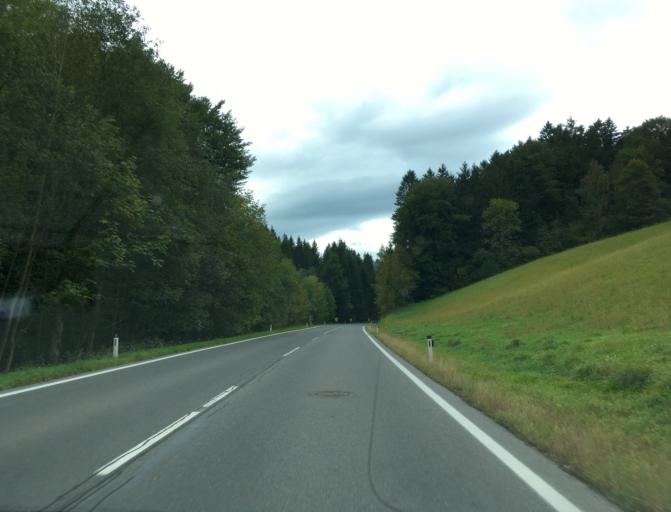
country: AT
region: Lower Austria
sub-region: Politischer Bezirk Neunkirchen
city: Thomasberg
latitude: 47.5594
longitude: 16.1431
